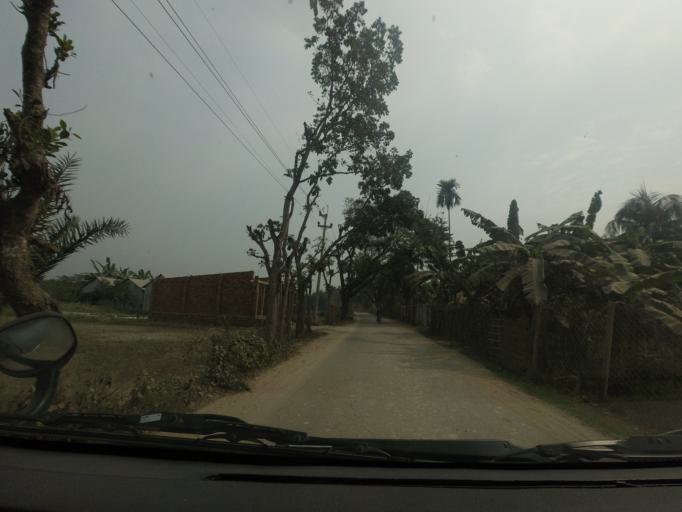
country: BD
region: Dhaka
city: Kishorganj
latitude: 24.3420
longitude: 90.7926
